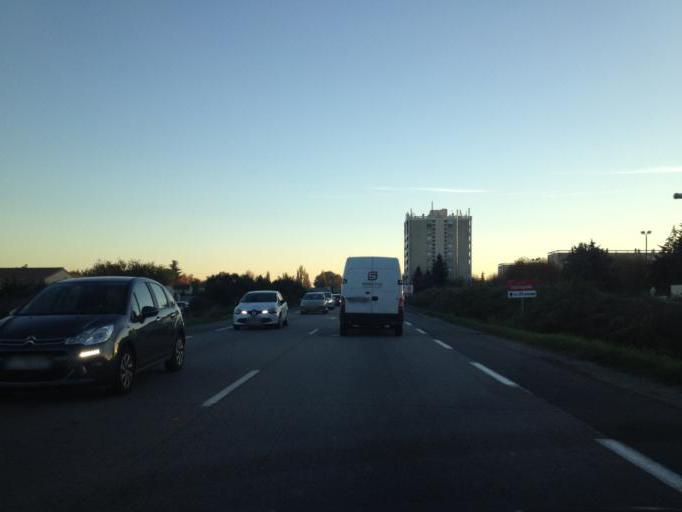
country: FR
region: Rhone-Alpes
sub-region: Departement de la Drome
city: Ancone
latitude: 44.5615
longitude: 4.7307
